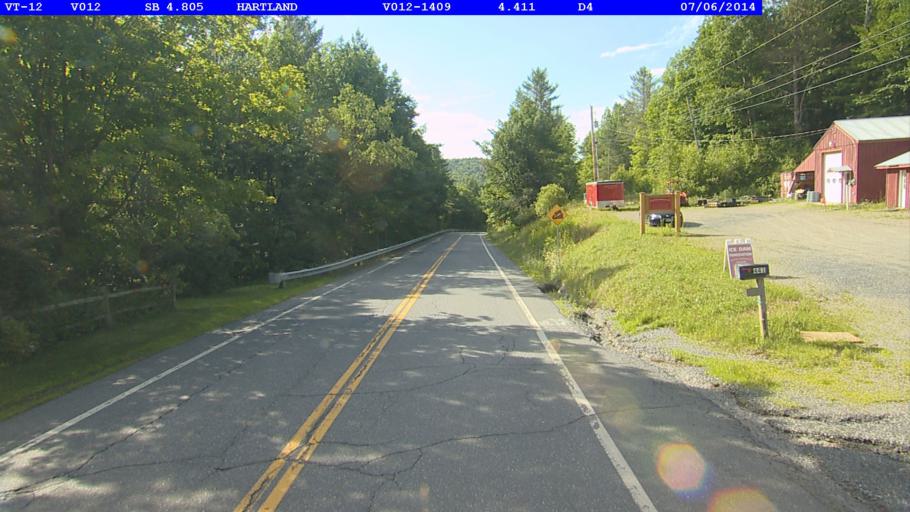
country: US
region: Vermont
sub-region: Windsor County
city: Woodstock
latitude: 43.5815
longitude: -72.4479
